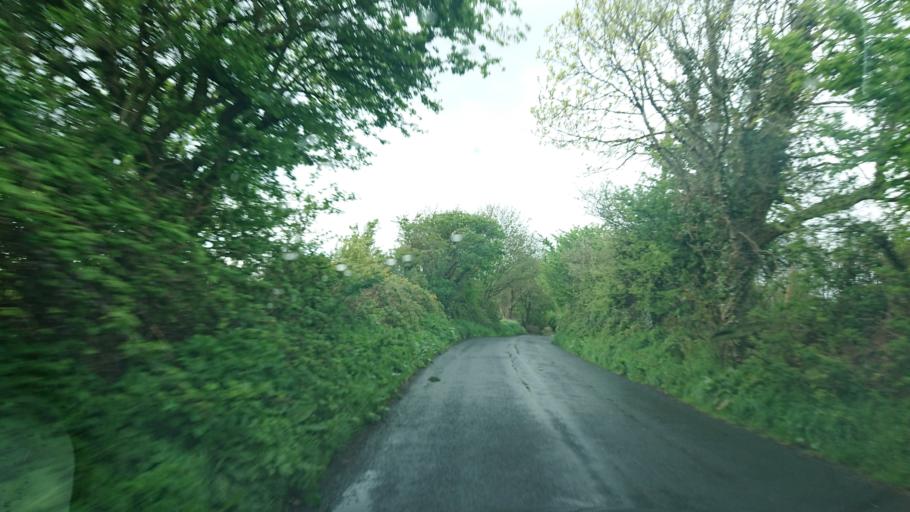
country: IE
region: Munster
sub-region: Waterford
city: Waterford
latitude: 52.2279
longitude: -7.0725
